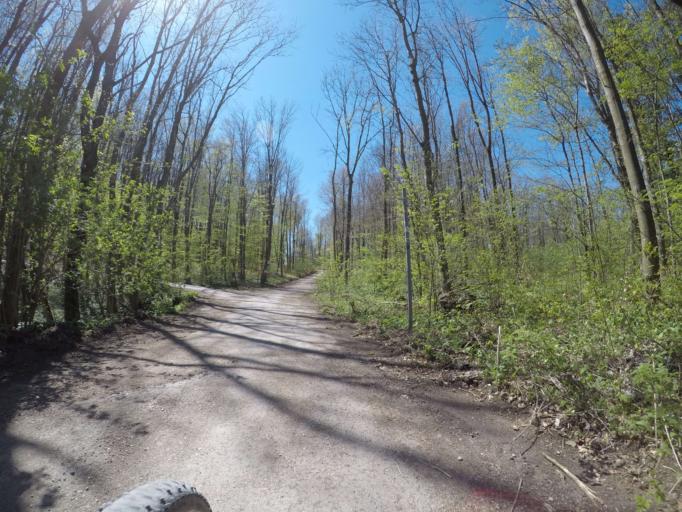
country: AT
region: Lower Austria
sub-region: Politischer Bezirk Modling
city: Hinterbruehl
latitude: 48.0544
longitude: 16.2463
